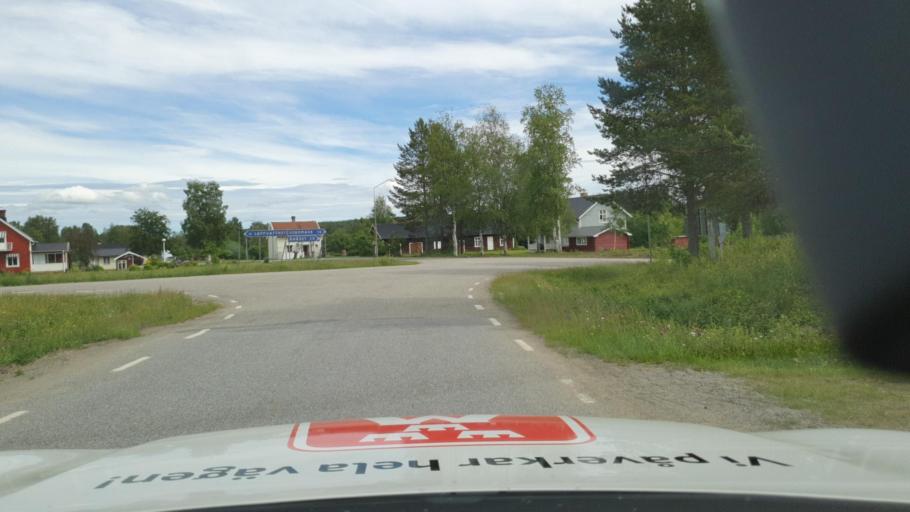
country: SE
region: Vaesterbotten
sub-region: Skelleftea Kommun
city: Burtraesk
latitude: 64.4976
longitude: 20.8575
